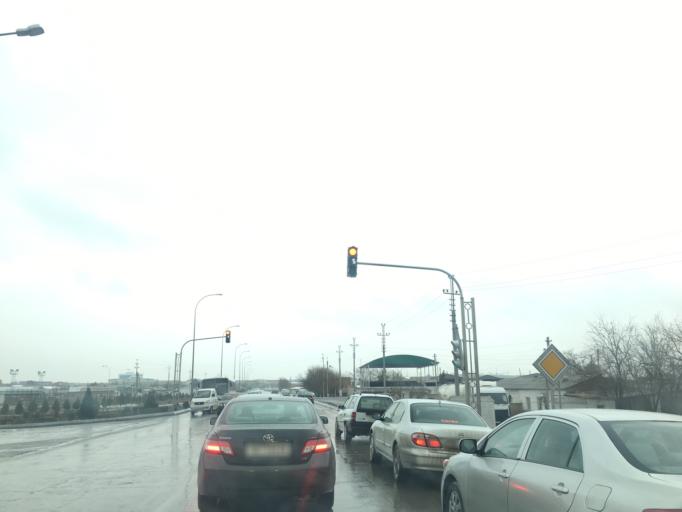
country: TM
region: Mary
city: Mary
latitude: 37.5788
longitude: 61.8354
